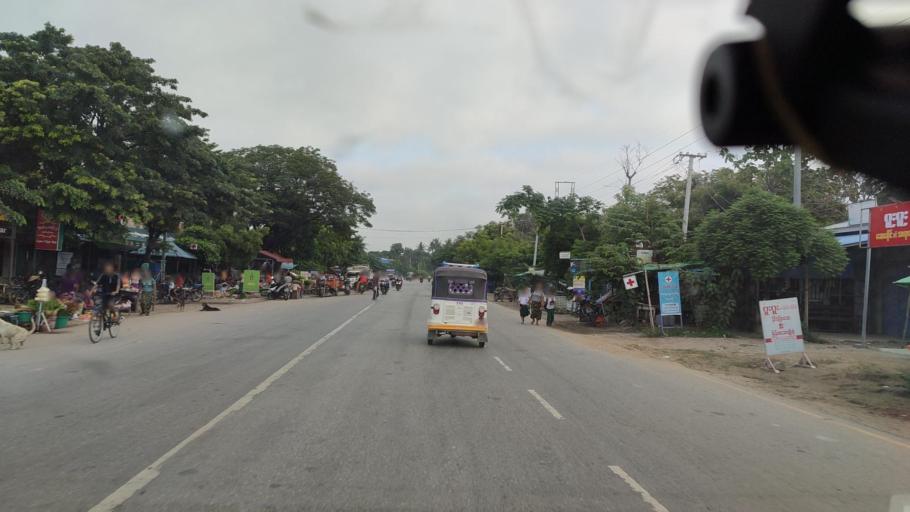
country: MM
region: Mandalay
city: Mandalay
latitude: 22.0871
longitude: 96.1467
